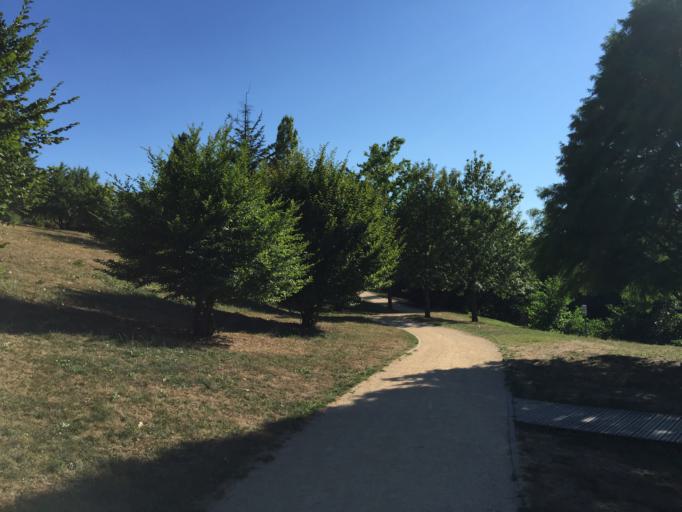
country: FR
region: Rhone-Alpes
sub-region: Departement de la Loire
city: Lorette
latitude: 45.5001
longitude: 4.5642
